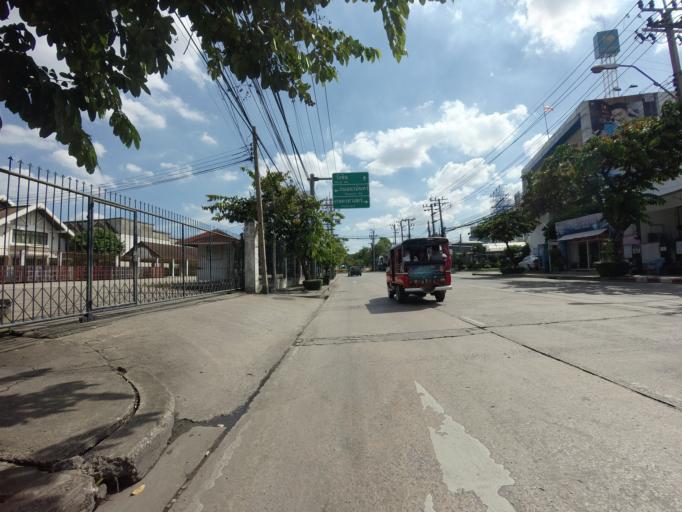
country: TH
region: Bangkok
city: Chatuchak
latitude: 13.8423
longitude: 100.5957
